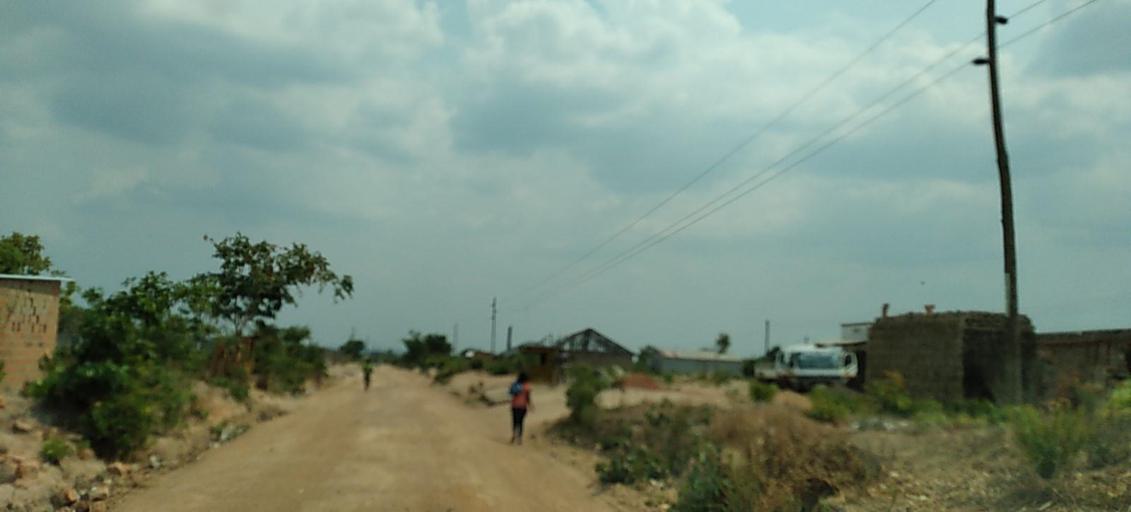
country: ZM
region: Copperbelt
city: Kalulushi
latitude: -12.8592
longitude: 28.0782
